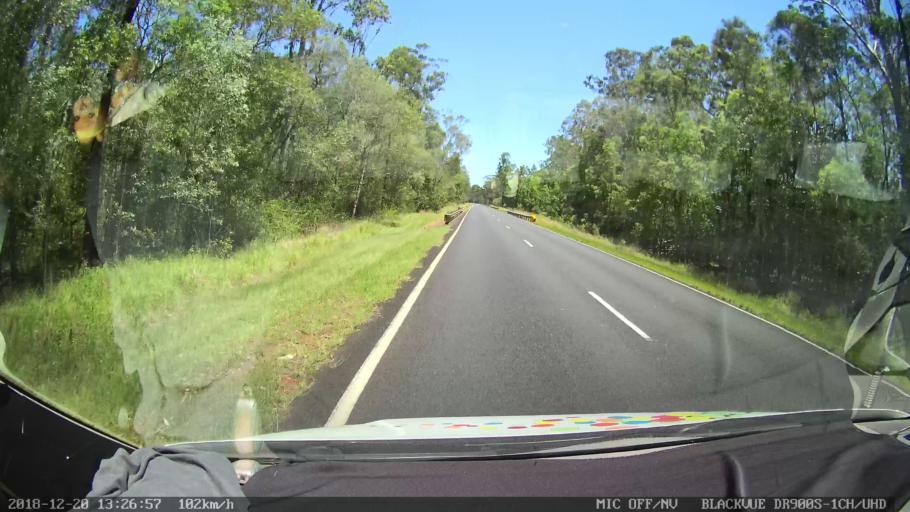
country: AU
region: New South Wales
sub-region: Richmond Valley
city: Casino
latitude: -29.1530
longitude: 152.9935
